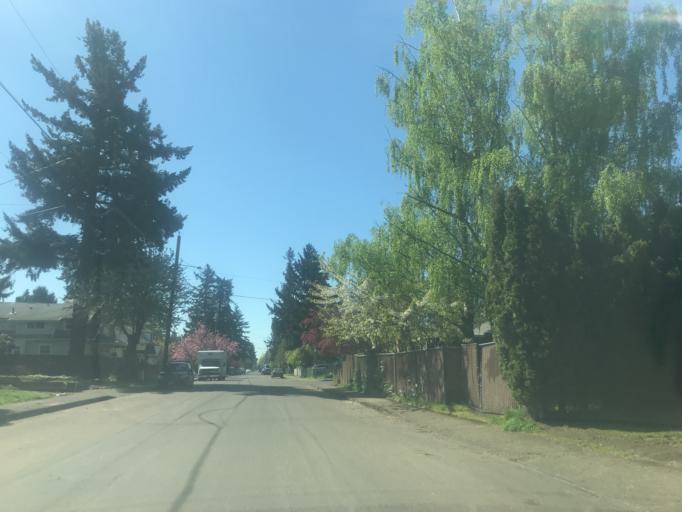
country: US
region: Oregon
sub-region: Multnomah County
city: Lents
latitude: 45.4852
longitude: -122.5996
